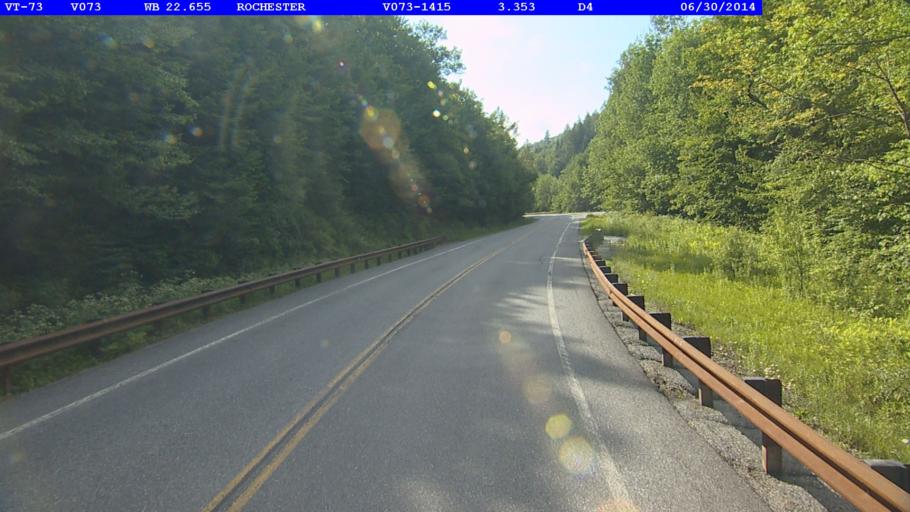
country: US
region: Vermont
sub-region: Rutland County
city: Brandon
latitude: 43.8519
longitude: -72.9041
